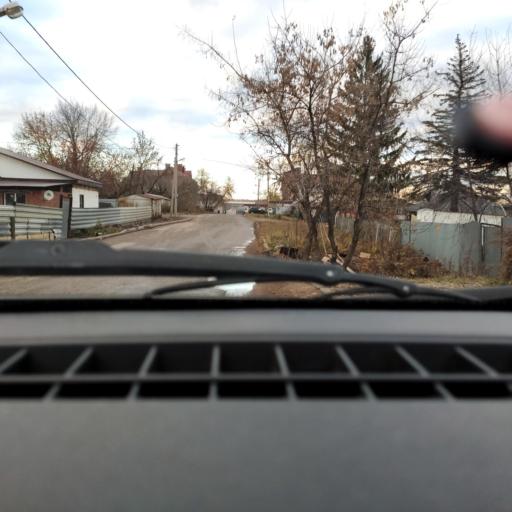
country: RU
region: Bashkortostan
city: Ufa
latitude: 54.8232
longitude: 56.1183
